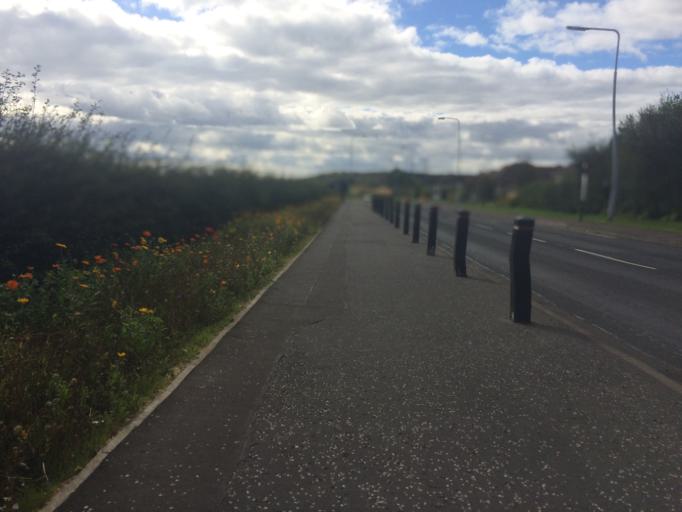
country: GB
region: Scotland
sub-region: Fife
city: Townhill
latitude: 56.0959
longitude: -3.4095
